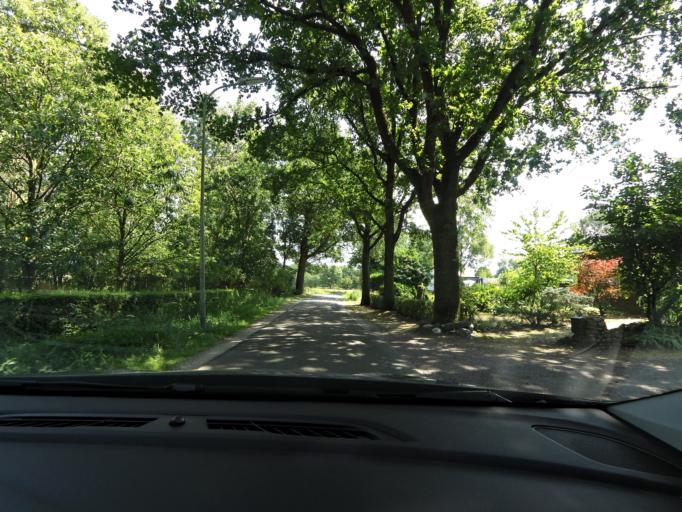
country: NL
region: Limburg
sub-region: Gemeente Leudal
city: Heythuysen
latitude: 51.2376
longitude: 5.8901
